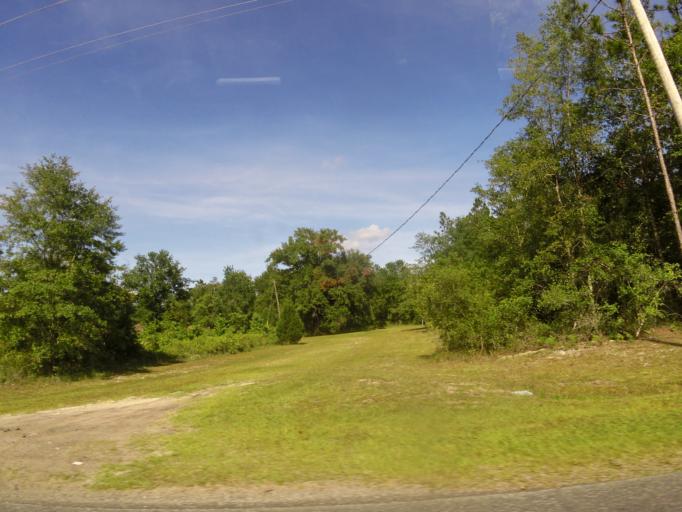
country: US
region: Florida
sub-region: Nassau County
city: Hilliard
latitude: 30.6722
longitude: -81.9045
